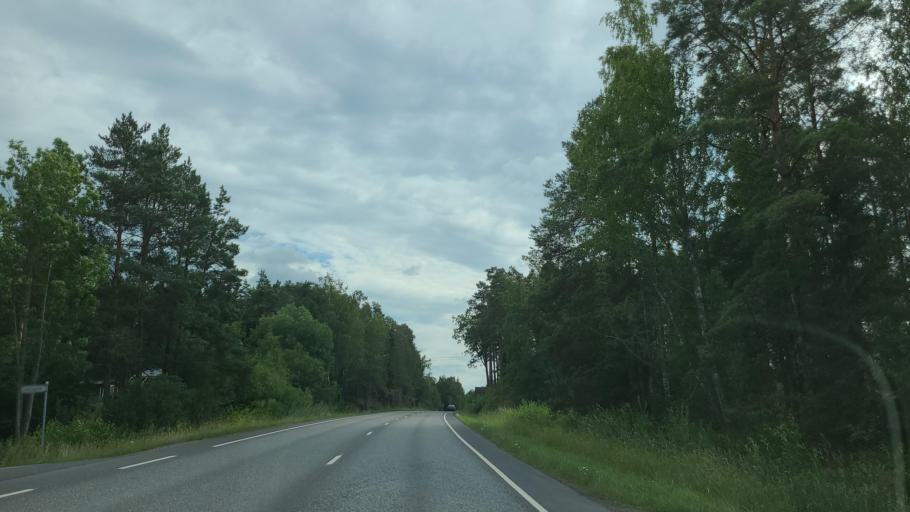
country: FI
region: Varsinais-Suomi
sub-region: Turku
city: Rymaettylae
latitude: 60.4250
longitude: 21.8973
